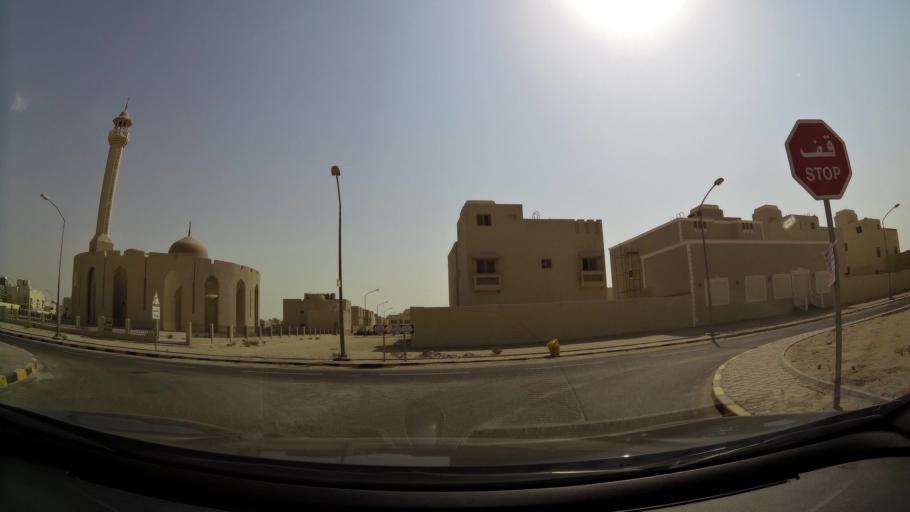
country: KW
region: Al Ahmadi
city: Al Wafrah
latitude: 28.8090
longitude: 48.0508
